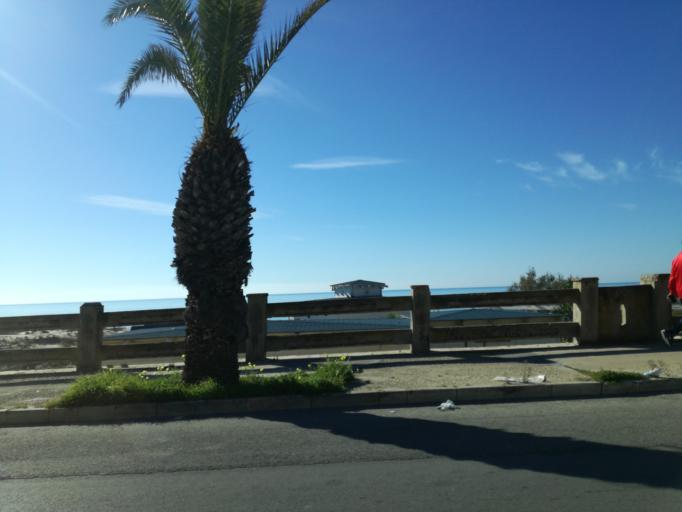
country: IT
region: Sicily
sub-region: Provincia di Caltanissetta
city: Gela
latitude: 37.0719
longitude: 14.2199
